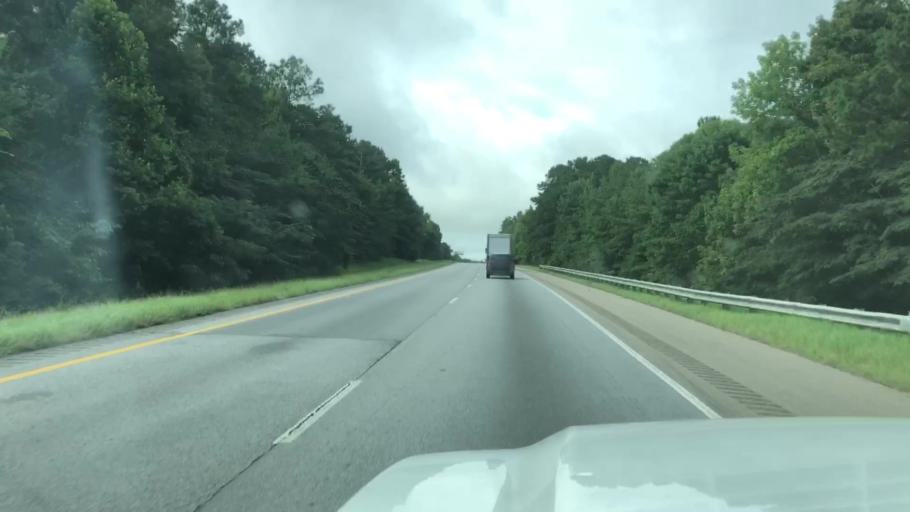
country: US
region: Alabama
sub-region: Lowndes County
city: Fort Deposit
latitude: 32.0019
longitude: -86.5245
